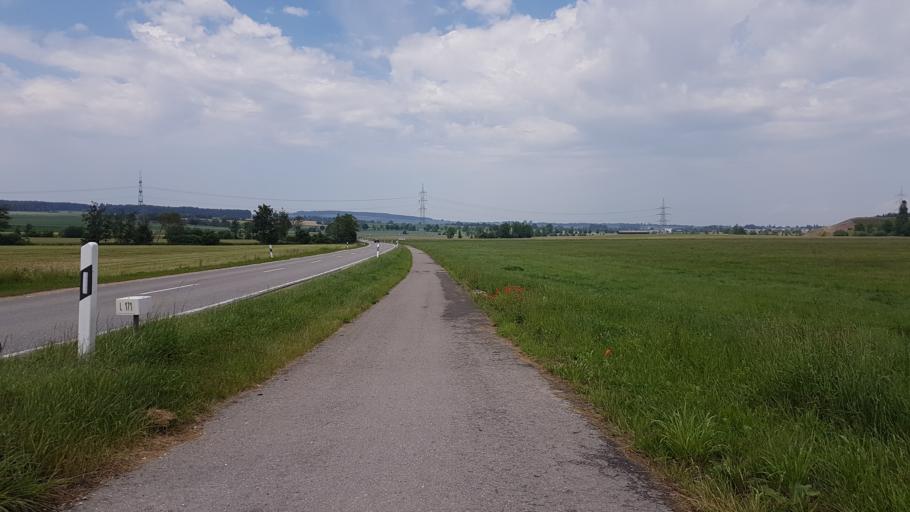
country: DE
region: Baden-Wuerttemberg
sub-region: Freiburg Region
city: Hufingen
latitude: 47.8986
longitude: 8.4873
